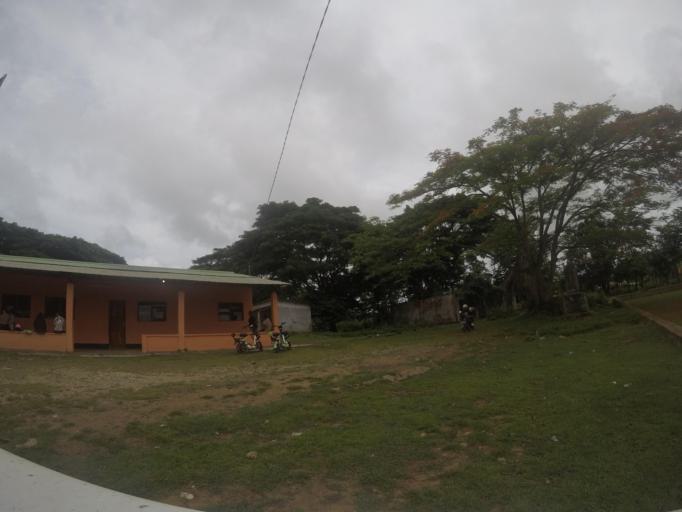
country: TL
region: Lautem
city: Lospalos
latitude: -8.5115
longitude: 126.9862
